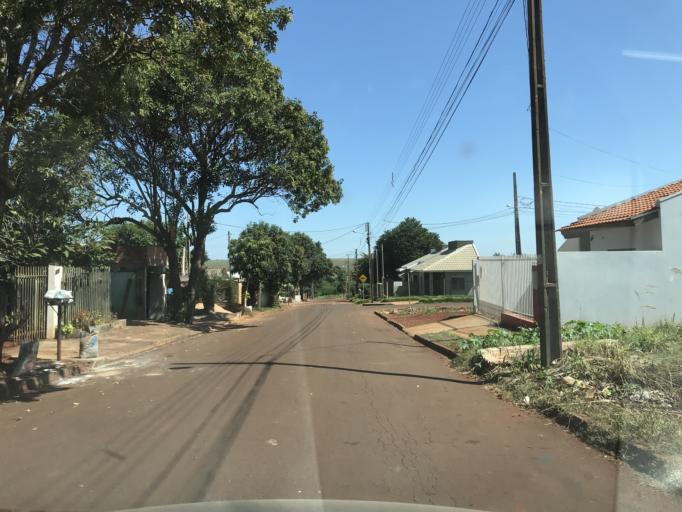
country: BR
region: Parana
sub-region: Palotina
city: Palotina
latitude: -24.2973
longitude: -53.8448
